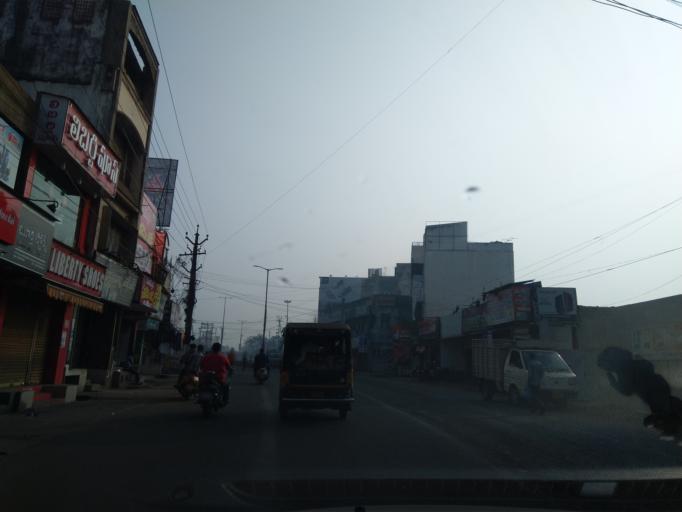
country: IN
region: Andhra Pradesh
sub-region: West Godavari
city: Bhimavaram
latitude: 16.5449
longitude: 81.5212
